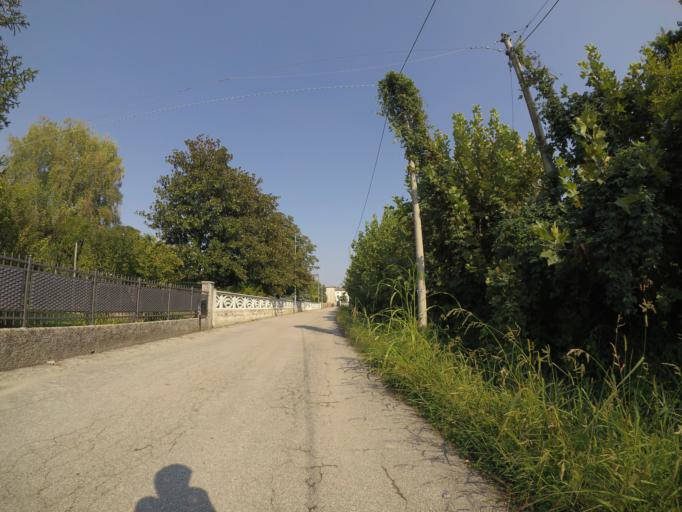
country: IT
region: Friuli Venezia Giulia
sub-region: Provincia di Udine
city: Varmo
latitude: 45.8855
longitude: 12.9832
